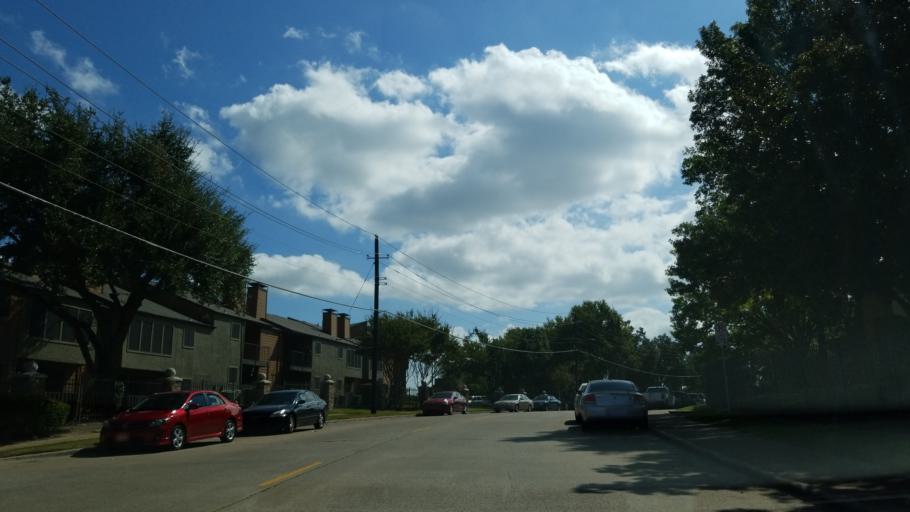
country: US
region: Texas
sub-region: Dallas County
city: Addison
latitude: 32.9432
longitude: -96.8100
